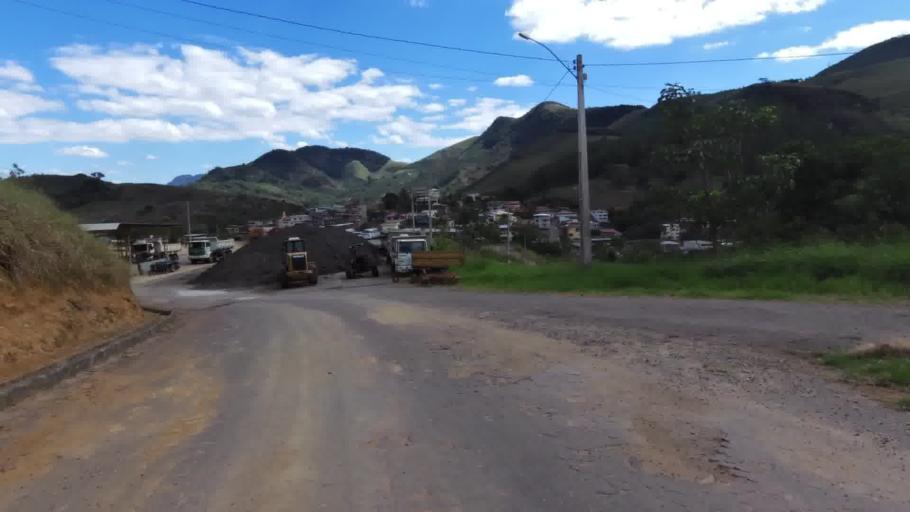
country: BR
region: Espirito Santo
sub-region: Rio Novo Do Sul
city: Rio Novo do Sul
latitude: -20.8690
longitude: -40.9388
